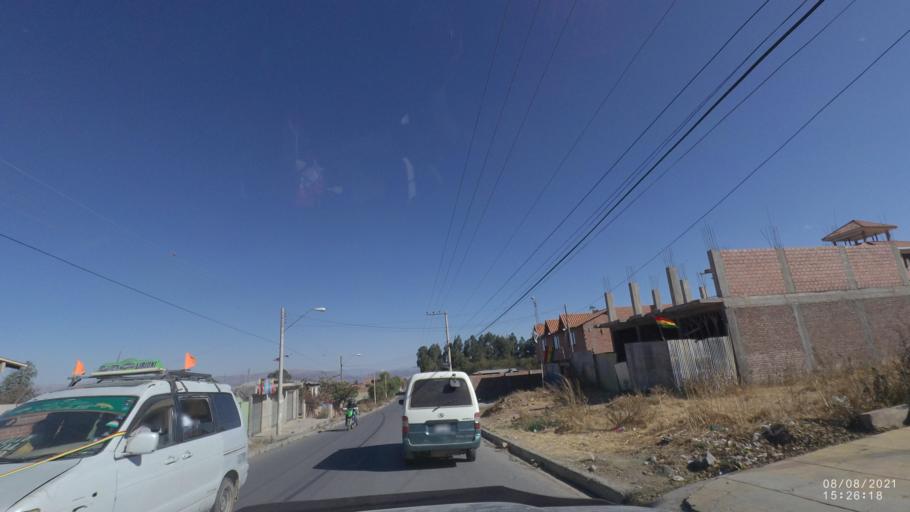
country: BO
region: Cochabamba
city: Cochabamba
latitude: -17.3223
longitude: -66.2817
